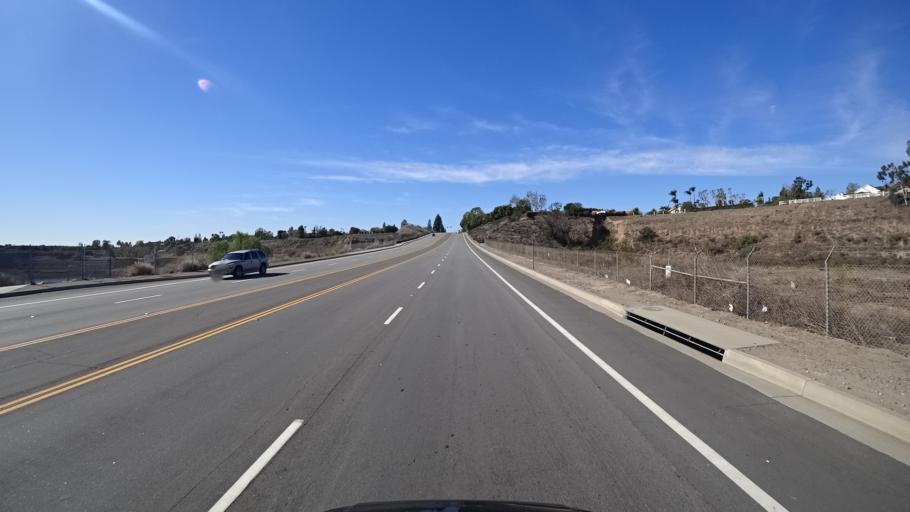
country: US
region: California
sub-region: Orange County
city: Villa Park
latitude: 33.8103
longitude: -117.8045
